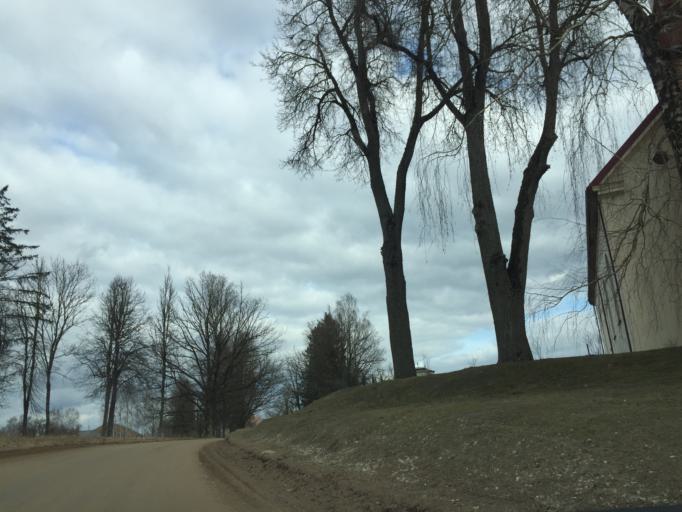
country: LV
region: Vecumnieki
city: Vecumnieki
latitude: 56.5078
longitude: 24.7212
